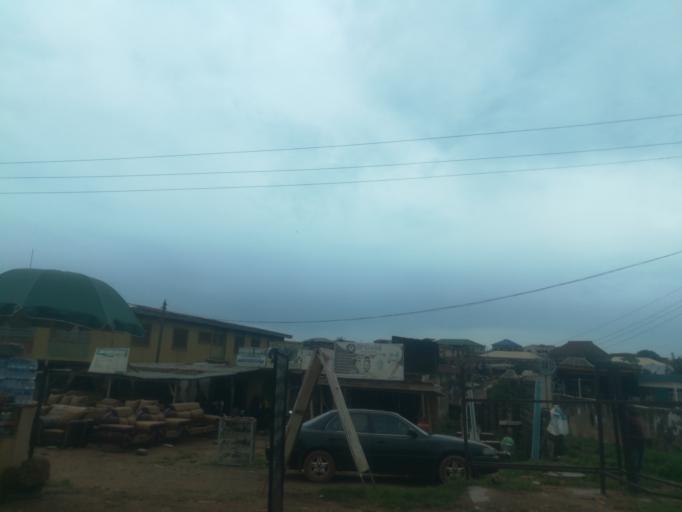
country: NG
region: Oyo
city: Ibadan
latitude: 7.3895
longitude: 3.9518
